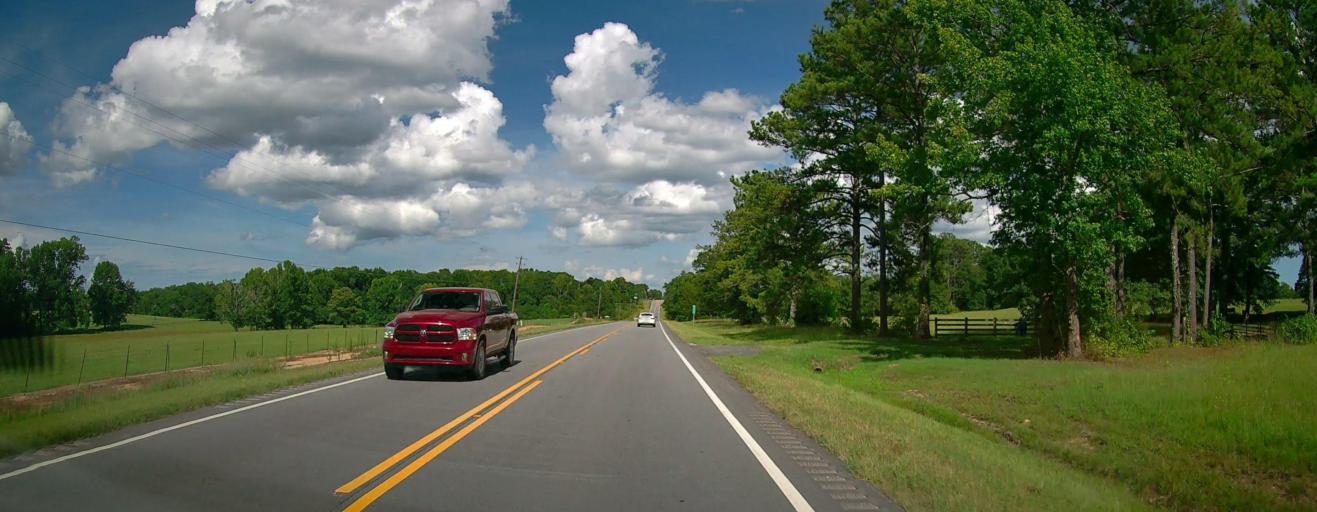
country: US
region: Alabama
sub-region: Lee County
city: Auburn
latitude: 32.4389
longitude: -85.3740
